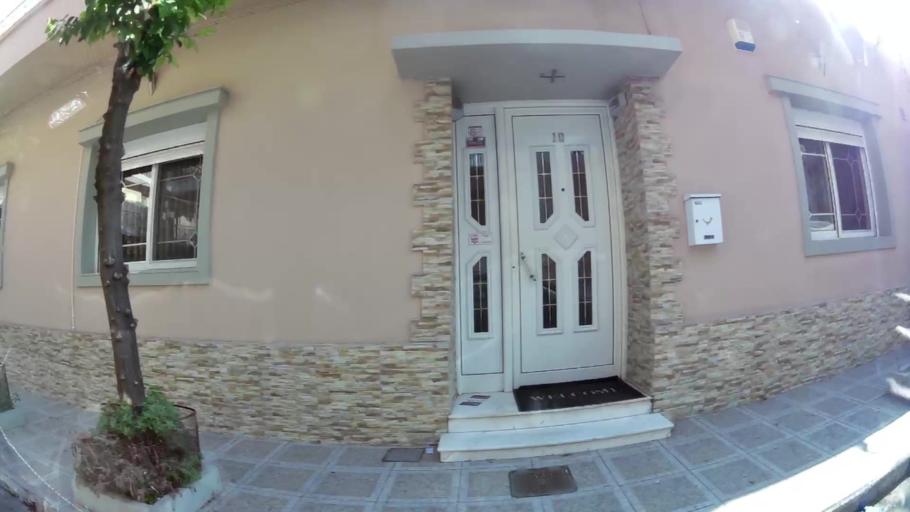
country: GR
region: Attica
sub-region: Nomos Piraios
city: Drapetsona
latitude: 37.9542
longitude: 23.6286
